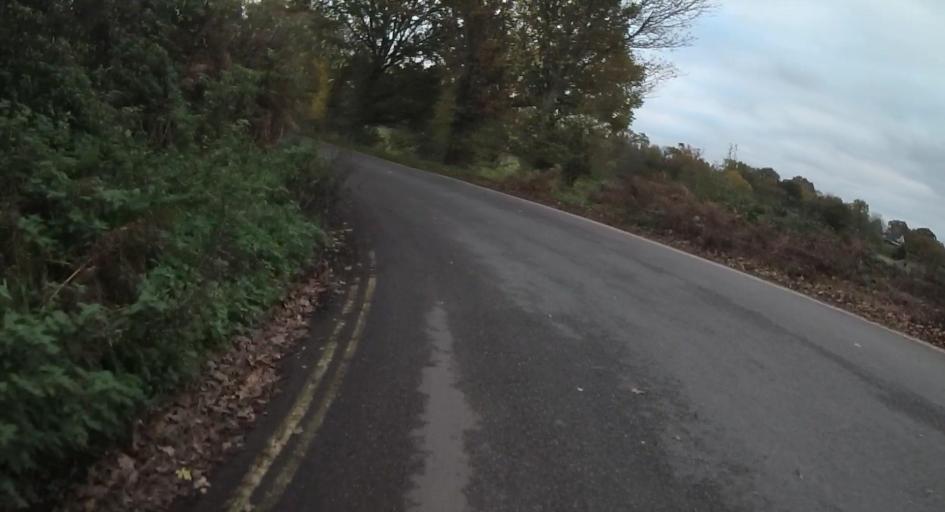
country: GB
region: England
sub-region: Surrey
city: Churt
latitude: 51.1503
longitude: -0.8002
